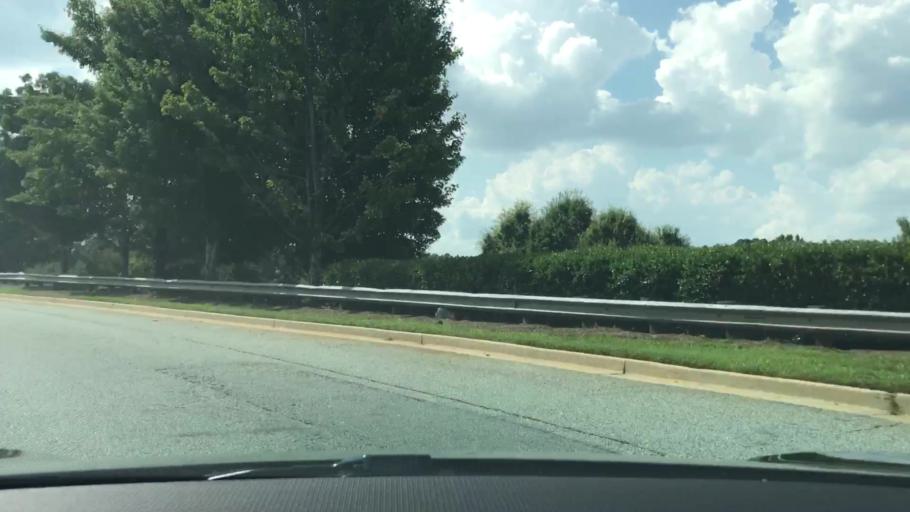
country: US
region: Georgia
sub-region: Gwinnett County
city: Suwanee
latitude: 34.0392
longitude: -84.0486
